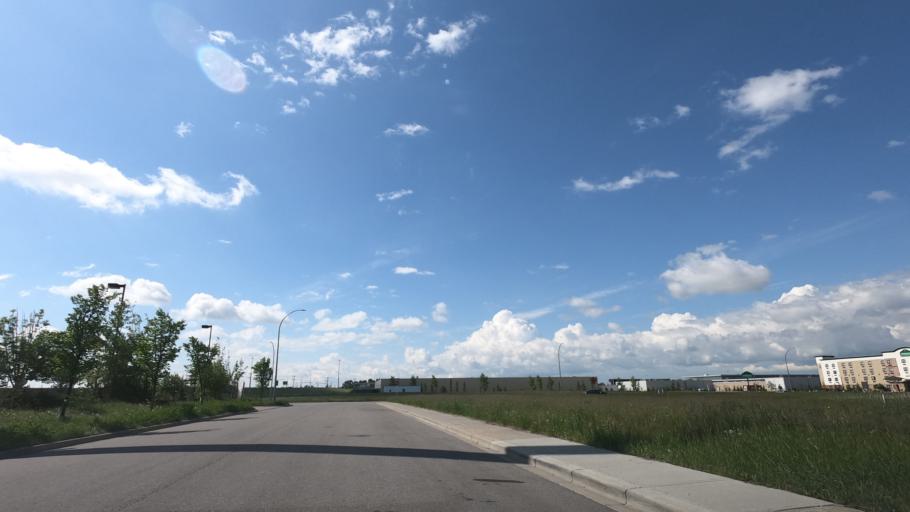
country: CA
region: Alberta
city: Airdrie
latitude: 51.3047
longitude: -114.0049
